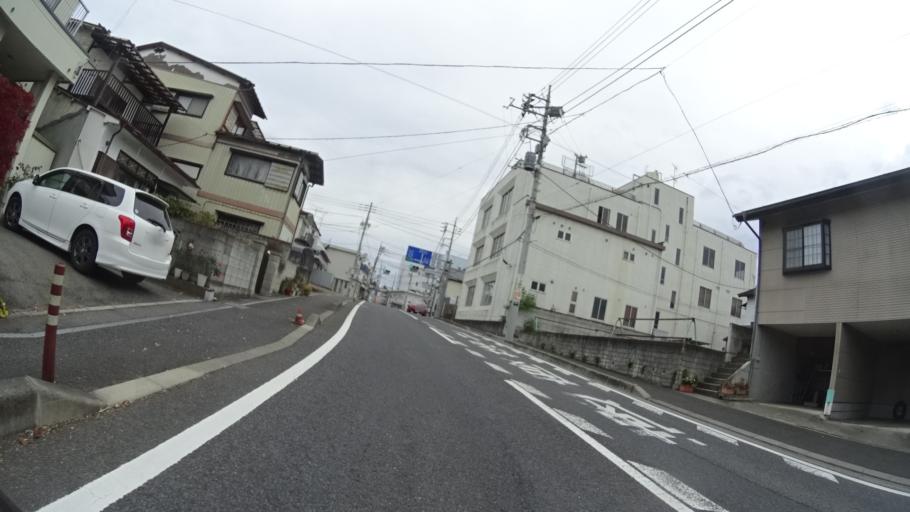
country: JP
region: Gunma
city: Numata
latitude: 36.6443
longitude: 139.0405
